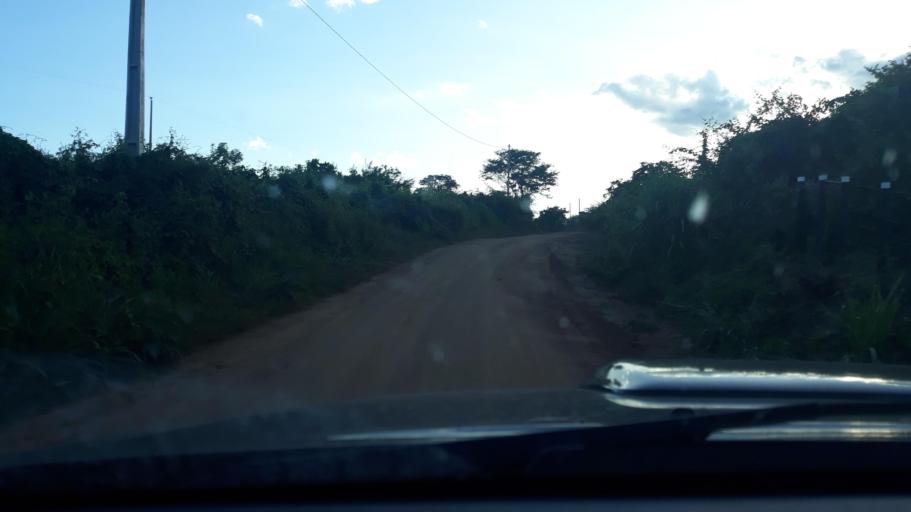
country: BR
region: Bahia
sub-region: Riacho De Santana
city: Riacho de Santana
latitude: -13.8073
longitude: -42.7159
